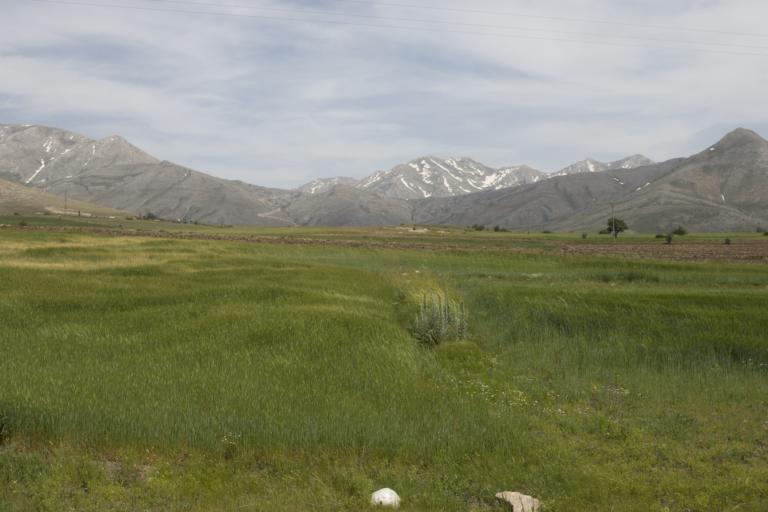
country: TR
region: Kayseri
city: Toklar
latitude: 38.4167
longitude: 36.0817
